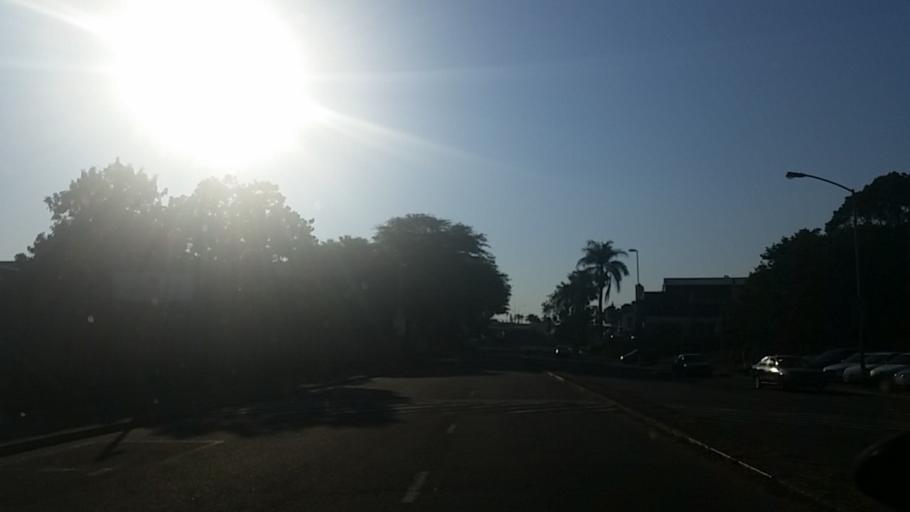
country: ZA
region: KwaZulu-Natal
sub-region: eThekwini Metropolitan Municipality
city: Berea
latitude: -29.8382
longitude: 30.9175
